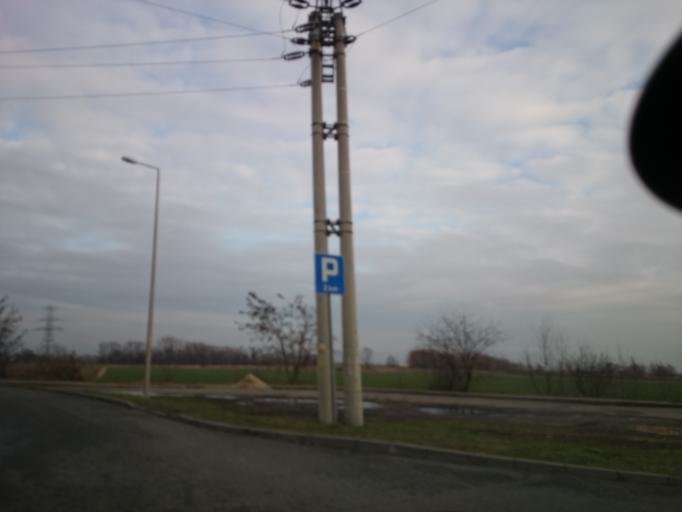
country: PL
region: Opole Voivodeship
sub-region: Powiat opolski
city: Opole
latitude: 50.6451
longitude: 17.9109
